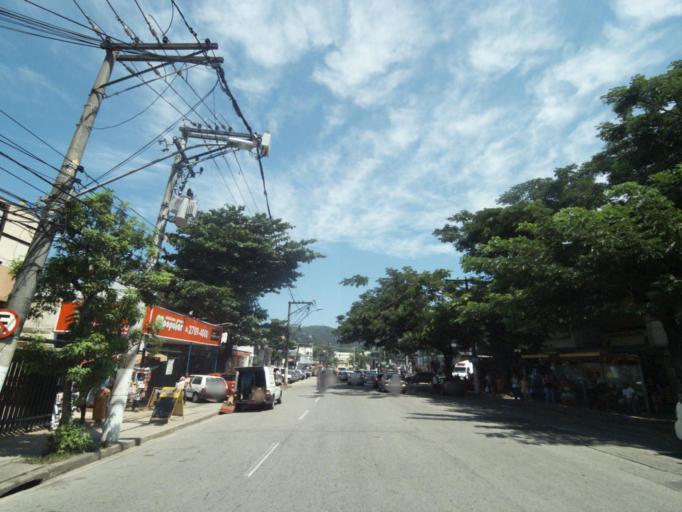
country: BR
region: Rio de Janeiro
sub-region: Niteroi
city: Niteroi
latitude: -22.9069
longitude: -43.0670
